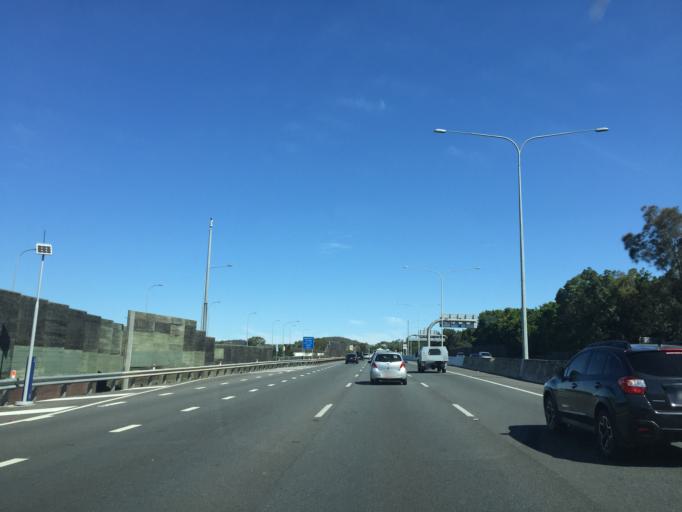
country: AU
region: Queensland
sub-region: Brisbane
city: Greenslopes
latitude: -27.5024
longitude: 153.0396
